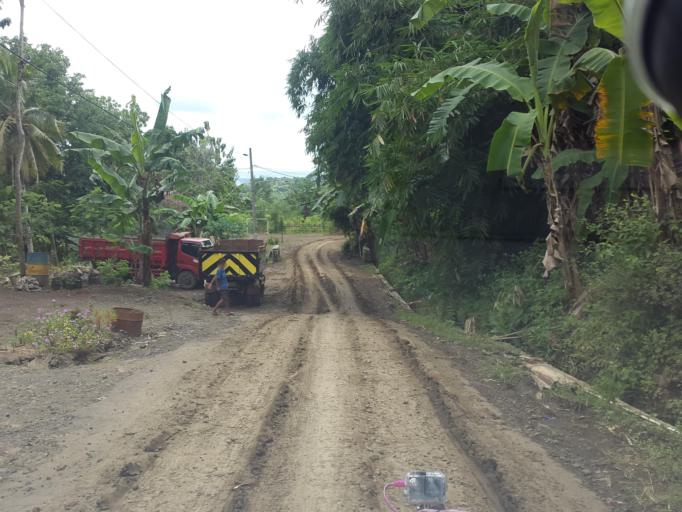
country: ID
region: Central Java
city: Watuagung
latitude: -7.5812
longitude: 109.1163
